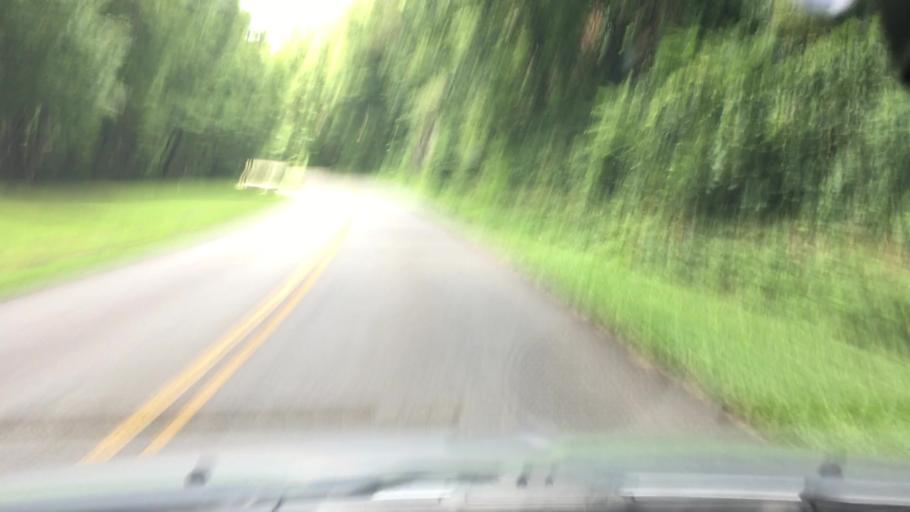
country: US
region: North Carolina
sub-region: Buncombe County
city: Asheville
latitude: 35.6233
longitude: -82.4922
